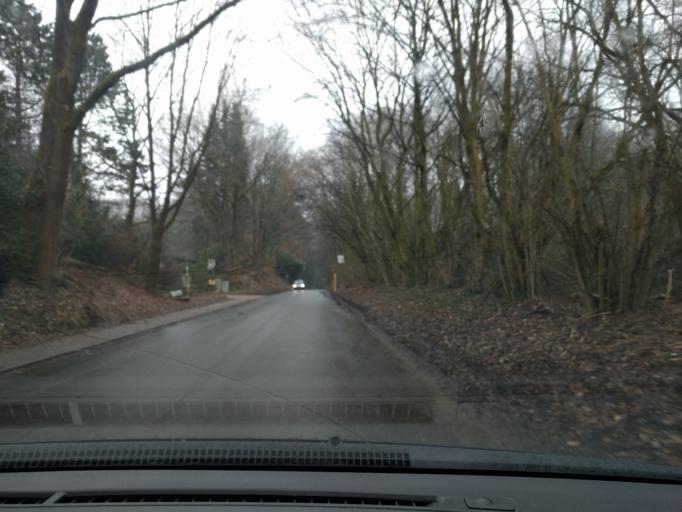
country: DE
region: Lower Saxony
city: Bendestorf
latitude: 53.3627
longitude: 9.9538
